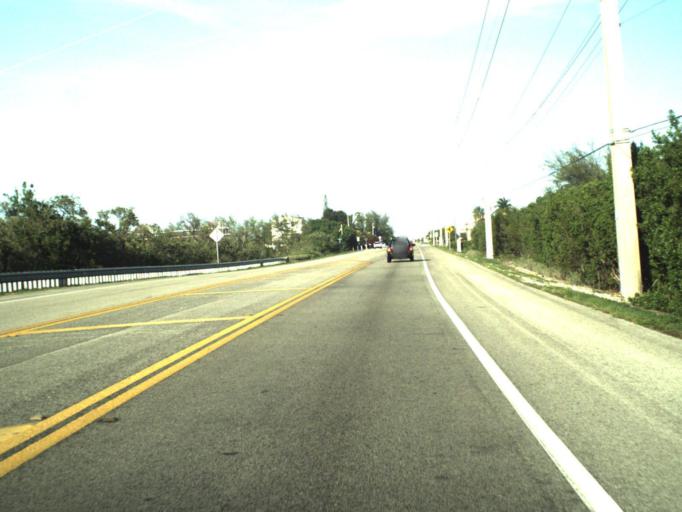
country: US
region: Florida
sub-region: Monroe County
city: Marathon
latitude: 24.7720
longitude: -80.9372
